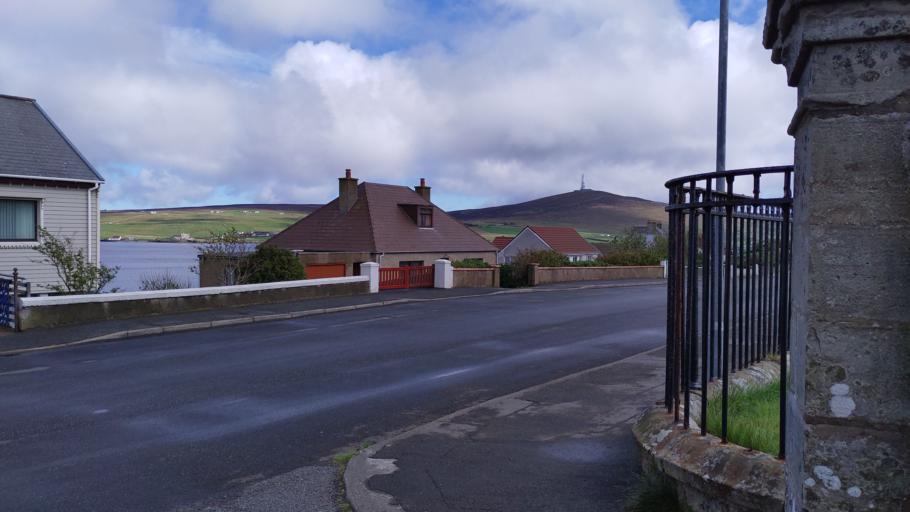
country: GB
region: Scotland
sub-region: Shetland Islands
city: Shetland
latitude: 60.1504
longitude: -1.1352
